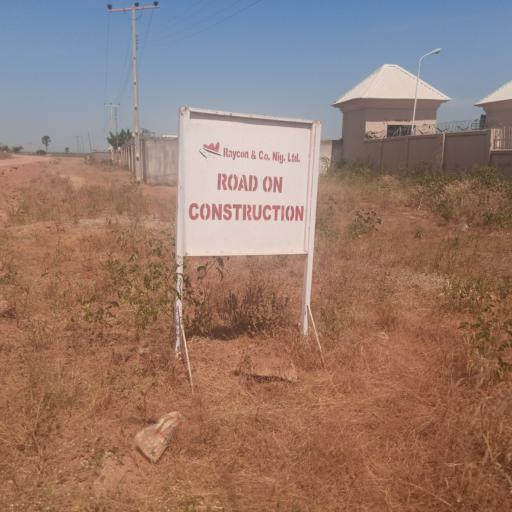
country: NG
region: Adamawa
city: Yola
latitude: 9.1150
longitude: 12.8764
